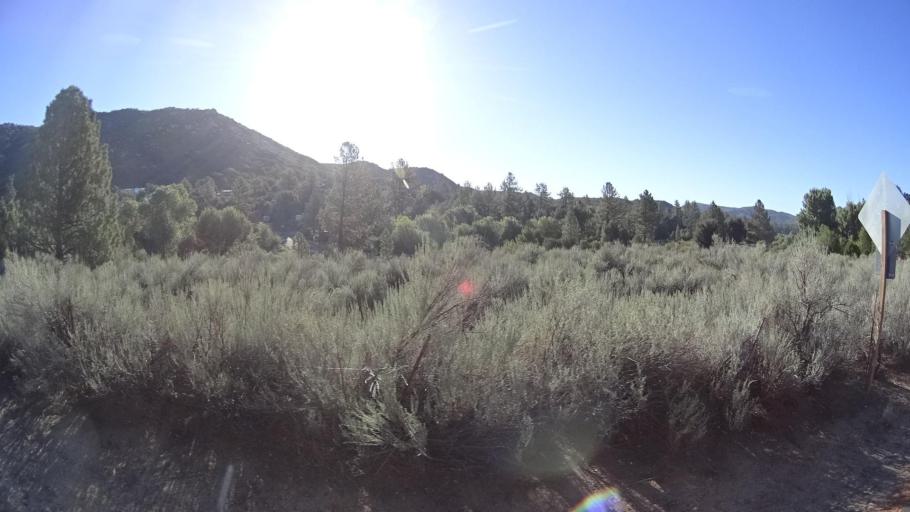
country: US
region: California
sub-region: San Diego County
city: Pine Valley
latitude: 32.8438
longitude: -116.5278
